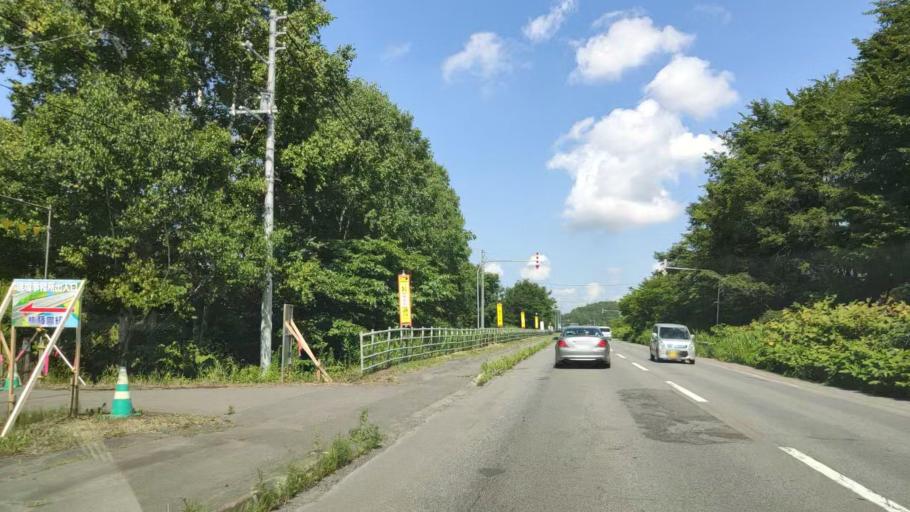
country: JP
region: Hokkaido
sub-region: Asahikawa-shi
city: Asahikawa
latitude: 43.6230
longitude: 142.4681
